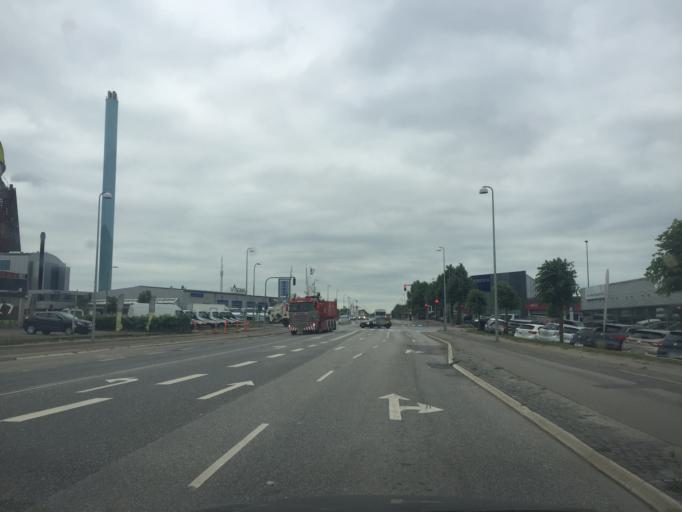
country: DK
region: Zealand
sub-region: Roskilde Kommune
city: Vindinge
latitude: 55.6434
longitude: 12.1255
